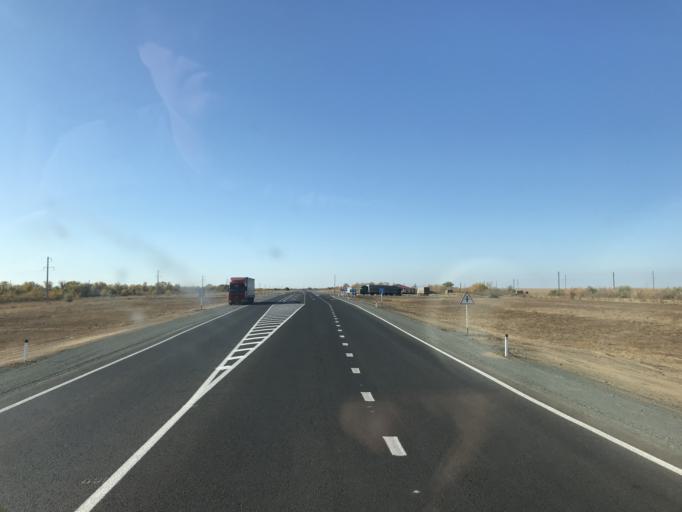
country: KZ
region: Pavlodar
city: Kurchatov
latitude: 51.4123
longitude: 78.2468
